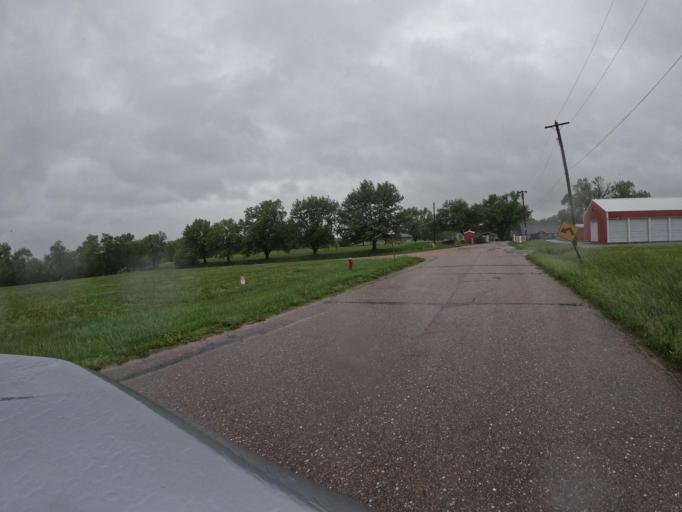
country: US
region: Nebraska
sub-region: Gage County
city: Wymore
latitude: 40.1193
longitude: -96.6815
